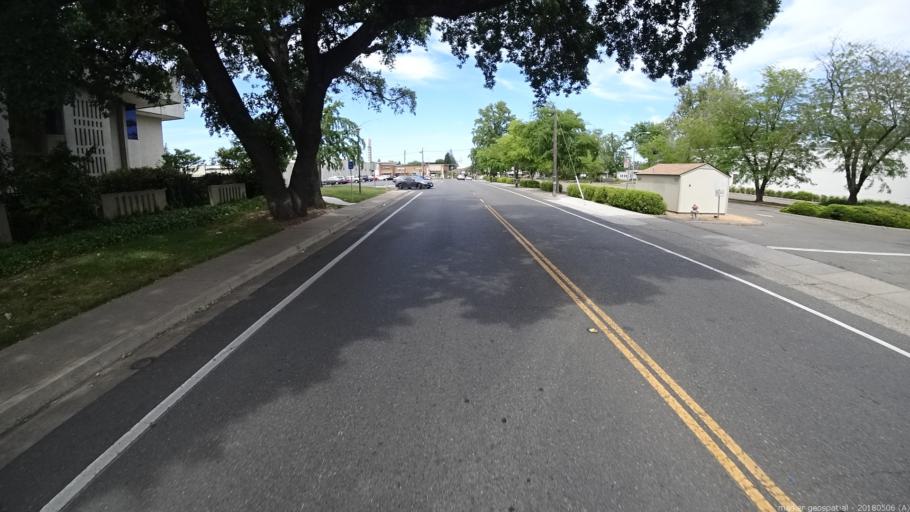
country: US
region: California
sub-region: Sacramento County
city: Sacramento
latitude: 38.5563
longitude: -121.4362
